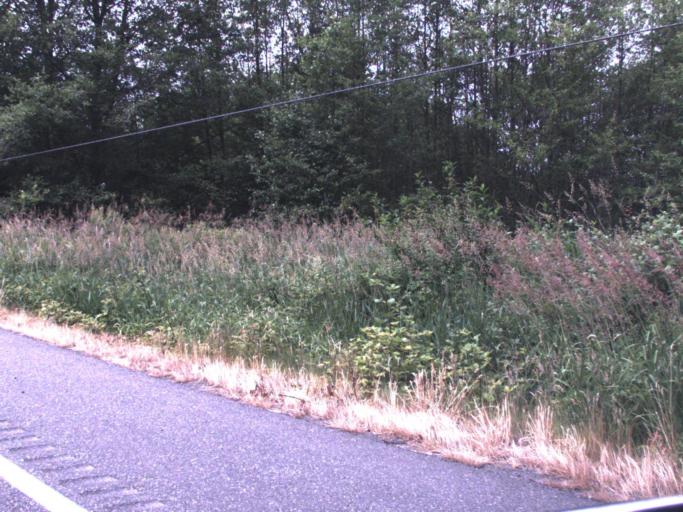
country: US
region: Washington
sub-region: Whatcom County
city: Birch Bay
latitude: 48.8920
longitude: -122.7168
